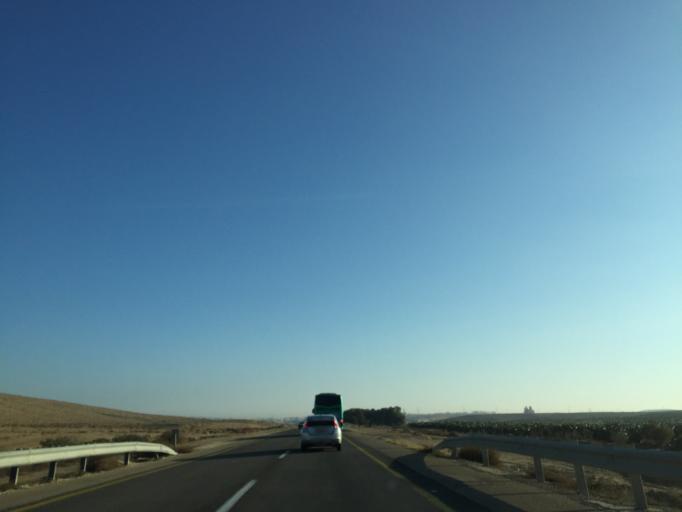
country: IL
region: Southern District
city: Dimona
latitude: 31.0489
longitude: 34.9884
